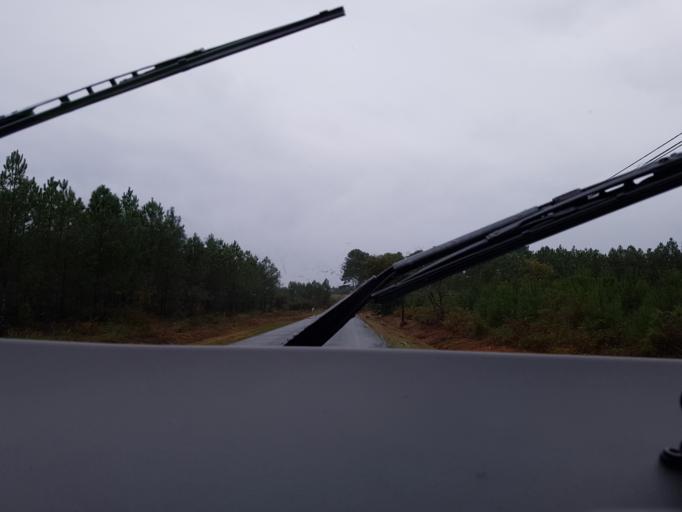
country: FR
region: Aquitaine
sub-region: Departement des Landes
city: Pissos
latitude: 44.3575
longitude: -0.6307
